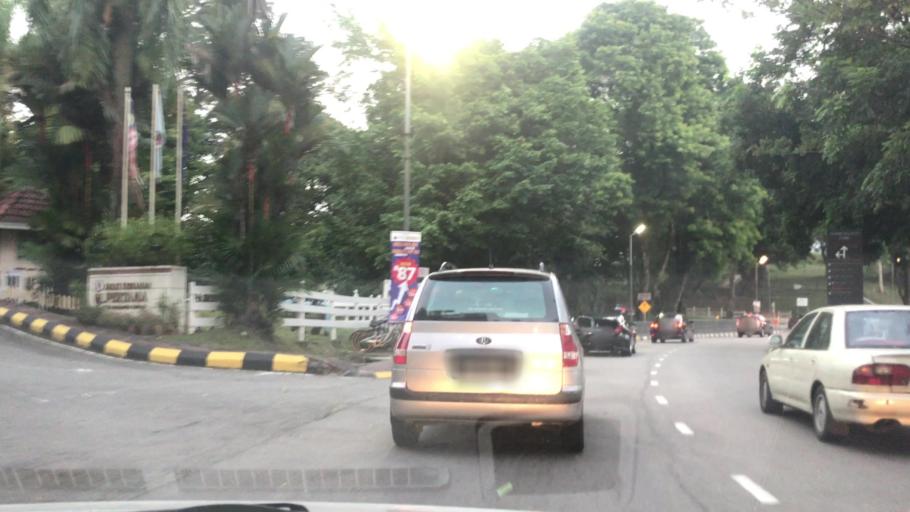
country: MY
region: Kuala Lumpur
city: Kuala Lumpur
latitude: 3.1183
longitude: 101.6597
